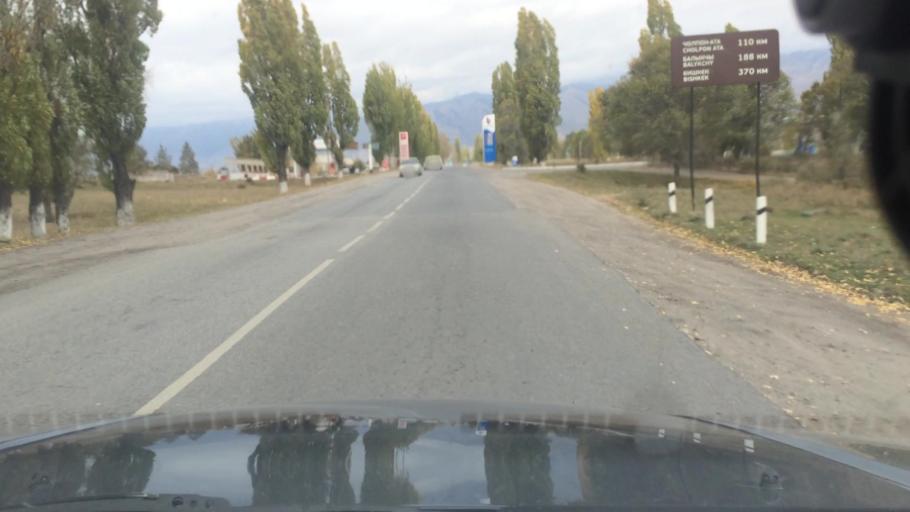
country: KG
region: Ysyk-Koel
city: Tyup
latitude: 42.7392
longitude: 78.3451
